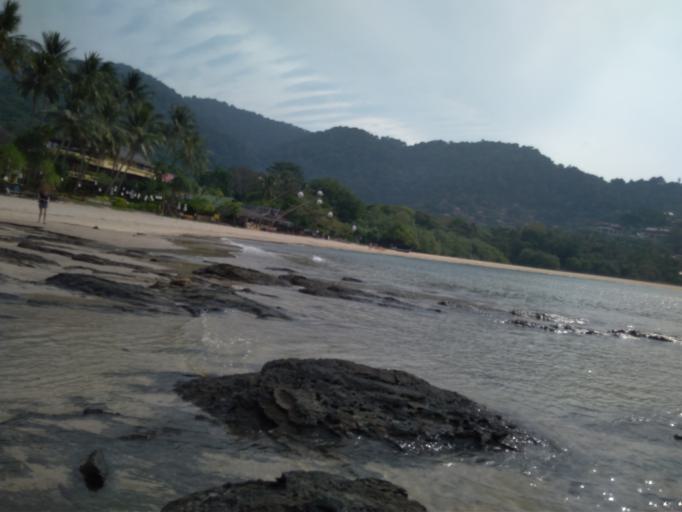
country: TH
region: Krabi
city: Ko Lanta
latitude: 7.4979
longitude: 99.0710
